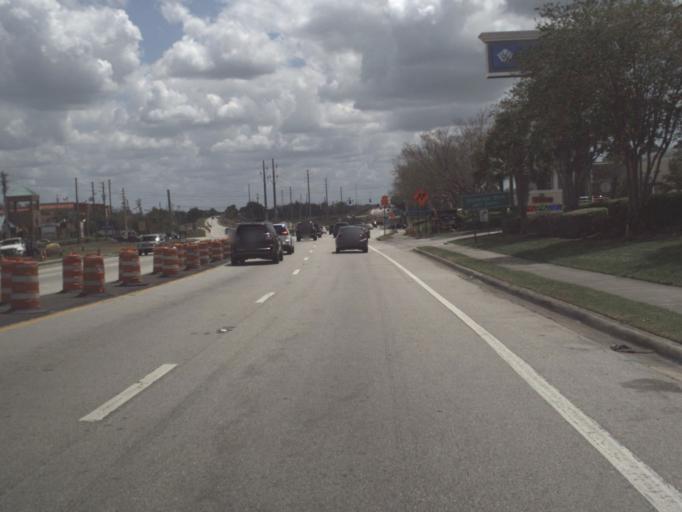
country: US
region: Florida
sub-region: Orange County
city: Tangelo Park
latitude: 28.4499
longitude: -81.4681
